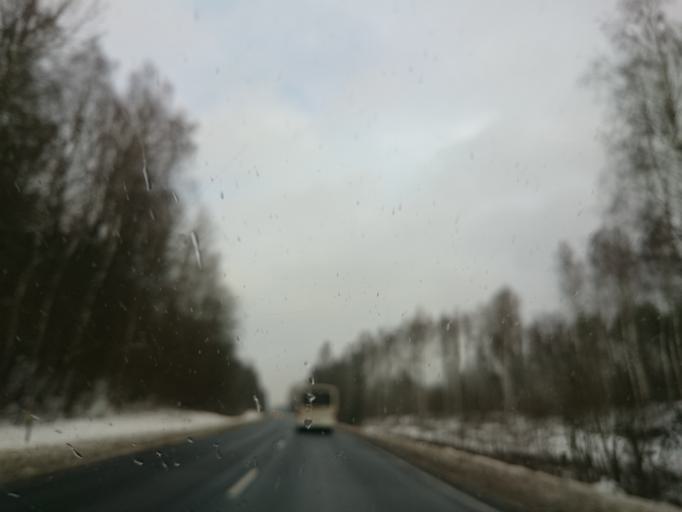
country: LV
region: Pargaujas
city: Stalbe
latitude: 57.3000
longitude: 24.9255
